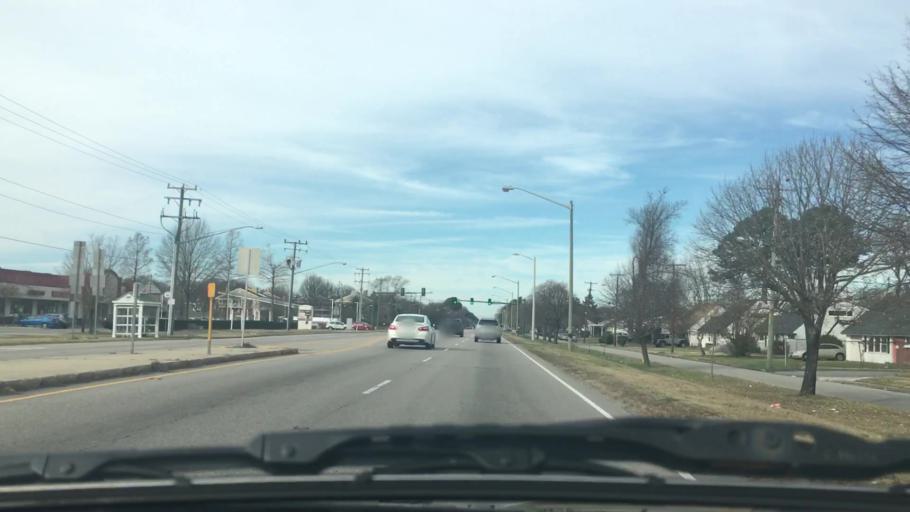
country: US
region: Virginia
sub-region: City of Norfolk
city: Norfolk
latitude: 36.8959
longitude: -76.2243
